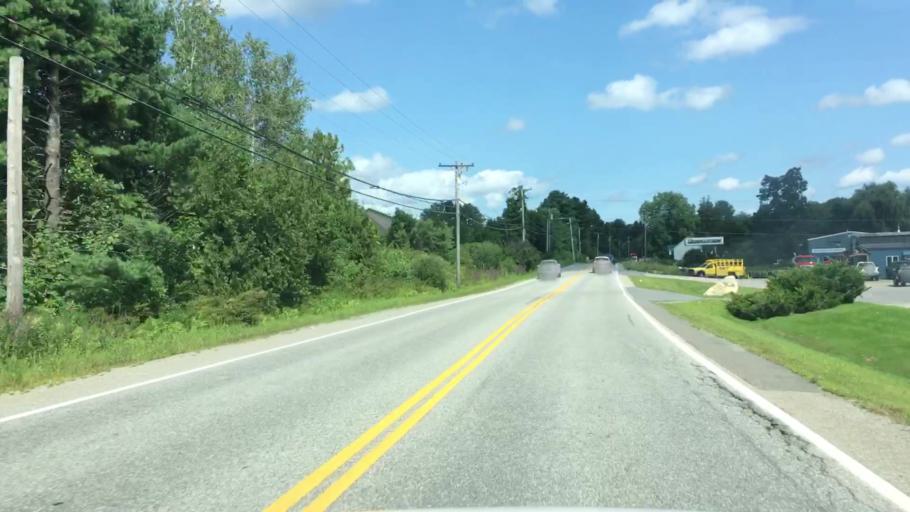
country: US
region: Maine
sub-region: Kennebec County
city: Augusta
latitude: 44.3255
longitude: -69.8178
